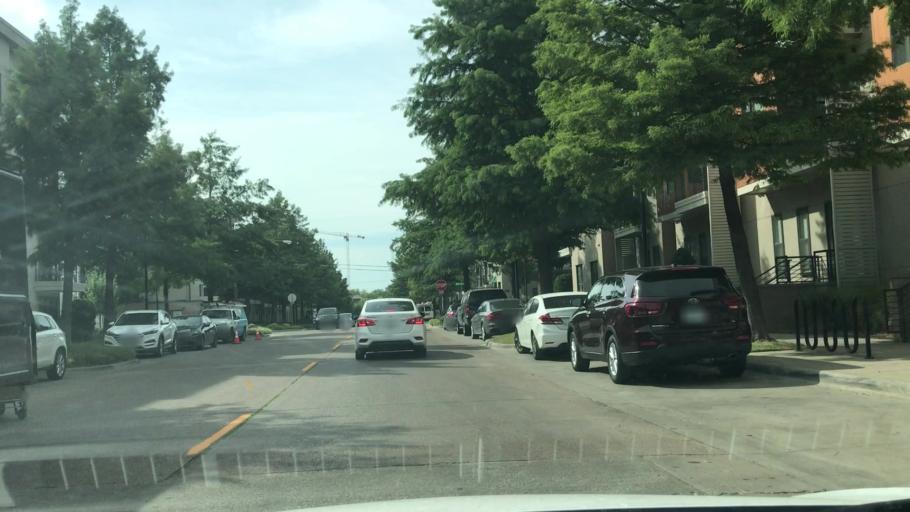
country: US
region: Texas
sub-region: Dallas County
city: Highland Park
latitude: 32.8127
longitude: -96.7816
